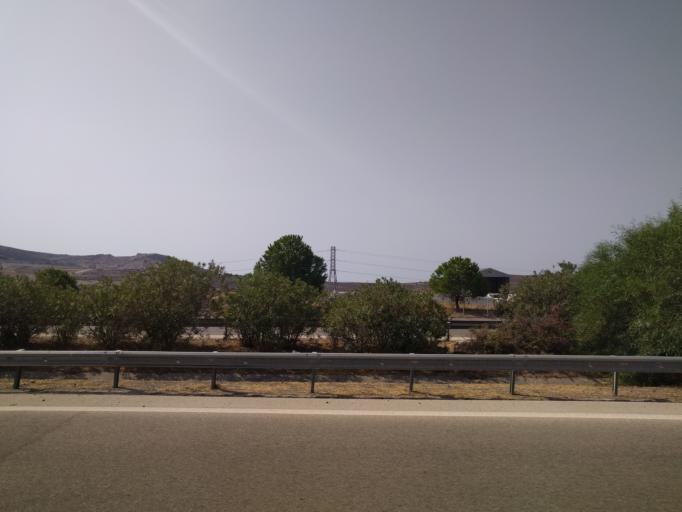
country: TR
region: Izmir
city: Alacati
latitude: 38.2783
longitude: 26.3920
